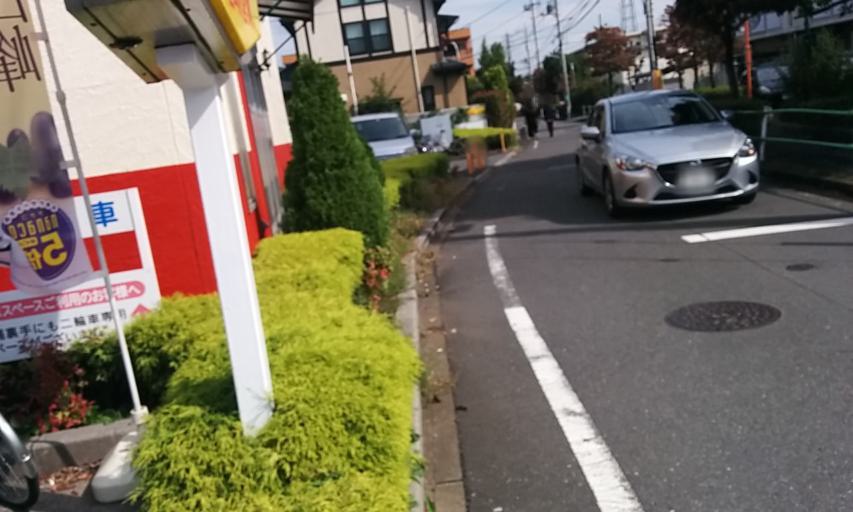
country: JP
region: Tokyo
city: Kokubunji
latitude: 35.6886
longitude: 139.4695
